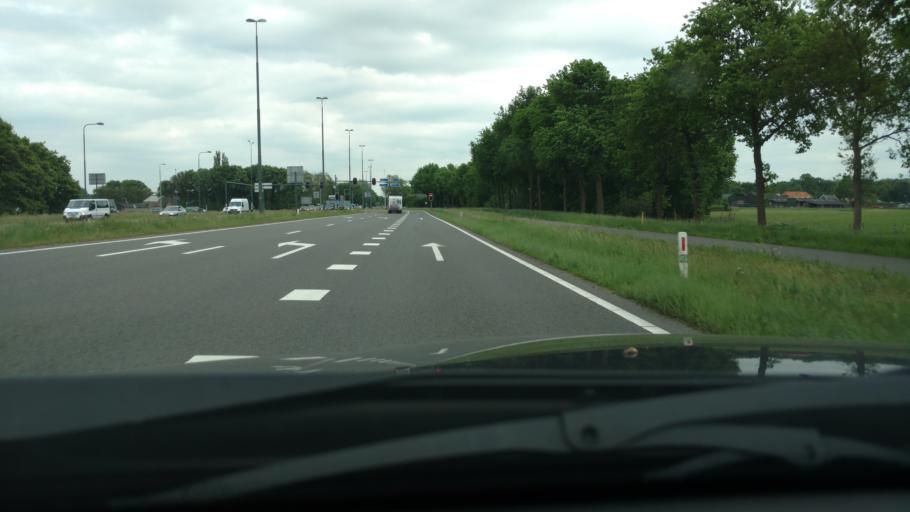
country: NL
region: Gelderland
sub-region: Gemeente Lochem
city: Epse
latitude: 52.2335
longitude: 6.1836
